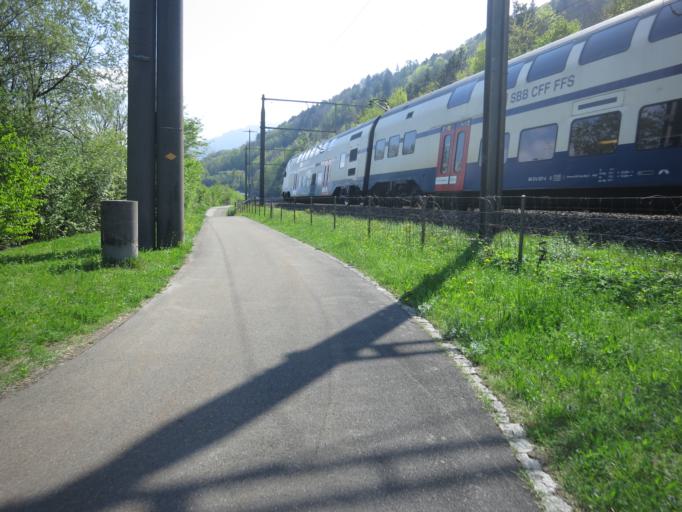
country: CH
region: Saint Gallen
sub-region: Wahlkreis Sarganserland
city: Quarten
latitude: 47.1142
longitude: 9.1993
